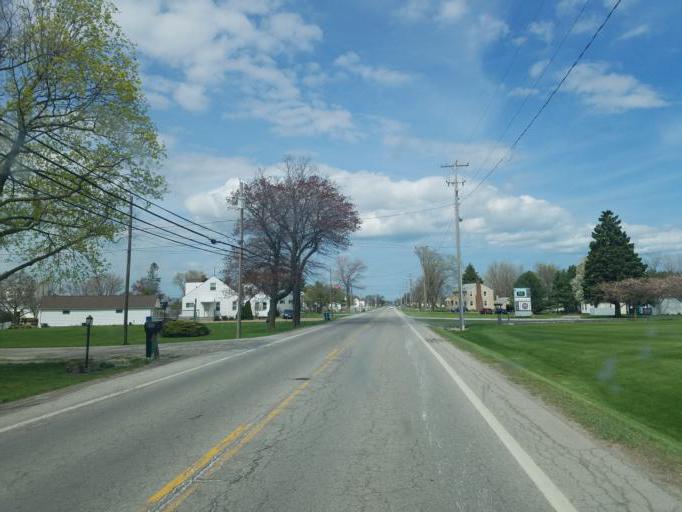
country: US
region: Ohio
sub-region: Erie County
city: Sandusky
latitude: 41.4172
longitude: -82.7225
